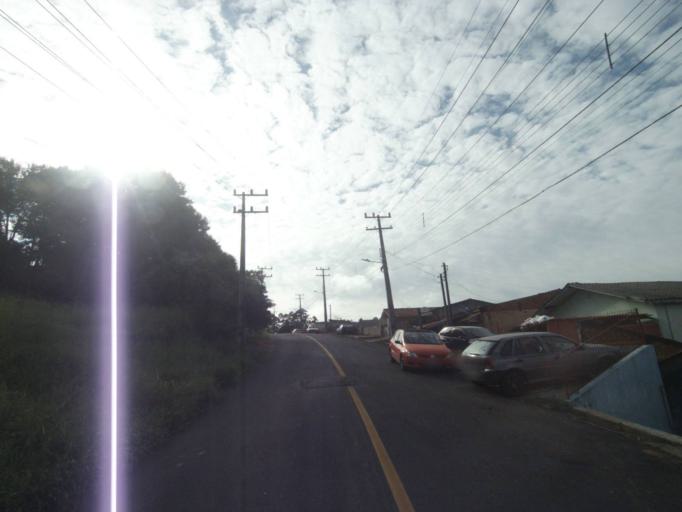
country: BR
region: Parana
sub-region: Telemaco Borba
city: Telemaco Borba
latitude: -24.3399
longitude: -50.6138
